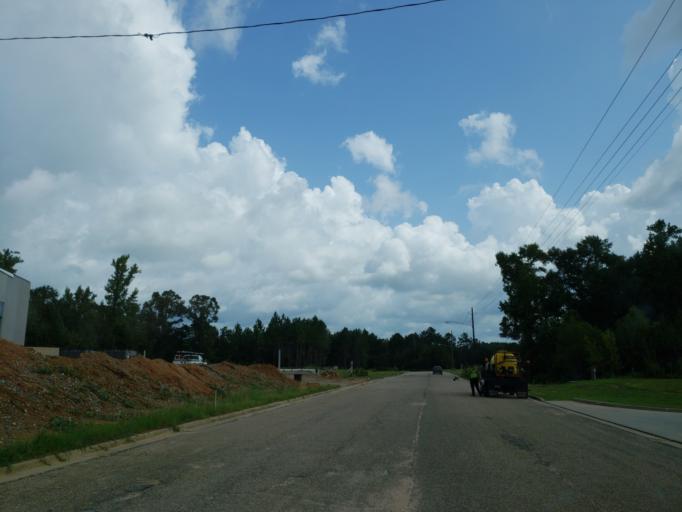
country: US
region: Mississippi
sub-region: Lamar County
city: West Hattiesburg
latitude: 31.3106
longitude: -89.3948
